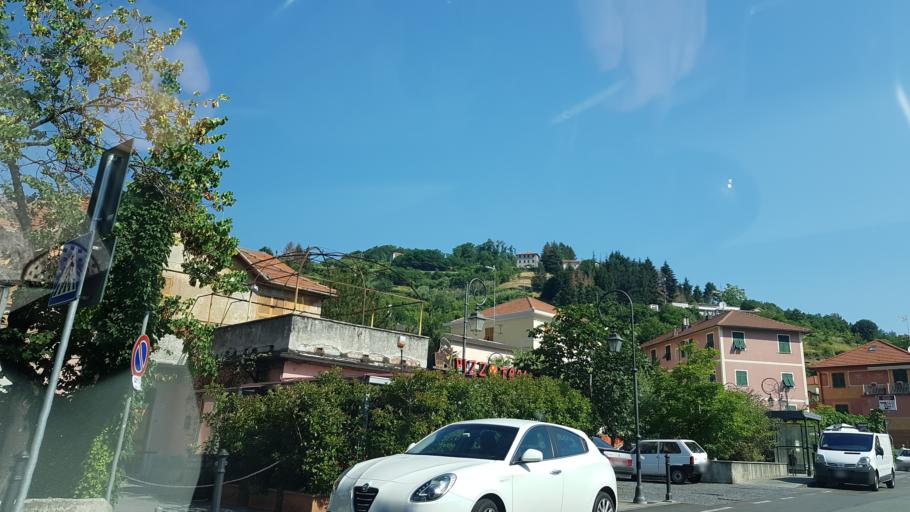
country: IT
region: Liguria
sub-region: Provincia di Genova
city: Serra Ricco
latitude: 44.5091
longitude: 8.9375
